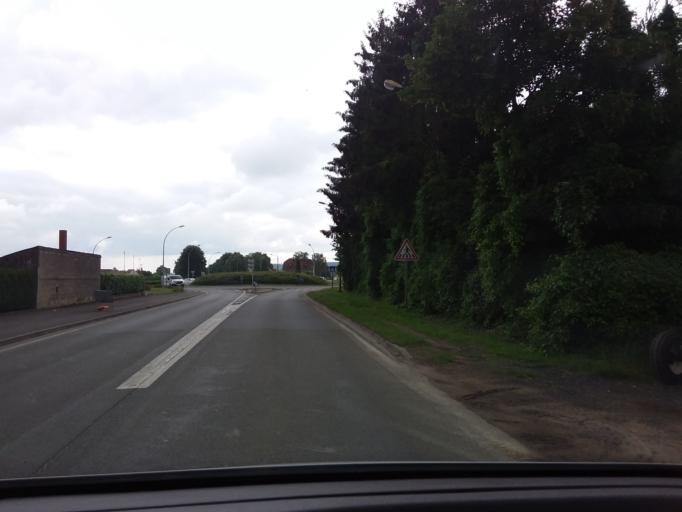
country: FR
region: Picardie
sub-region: Departement de l'Aisne
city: Bucy-le-Long
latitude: 49.3880
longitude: 3.3919
